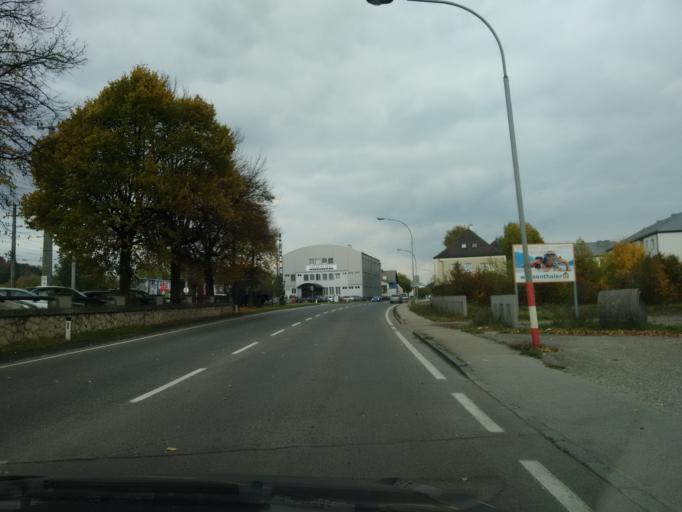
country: AT
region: Upper Austria
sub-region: Politischer Bezirk Vocklabruck
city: Redlham
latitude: 48.0151
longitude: 13.7238
